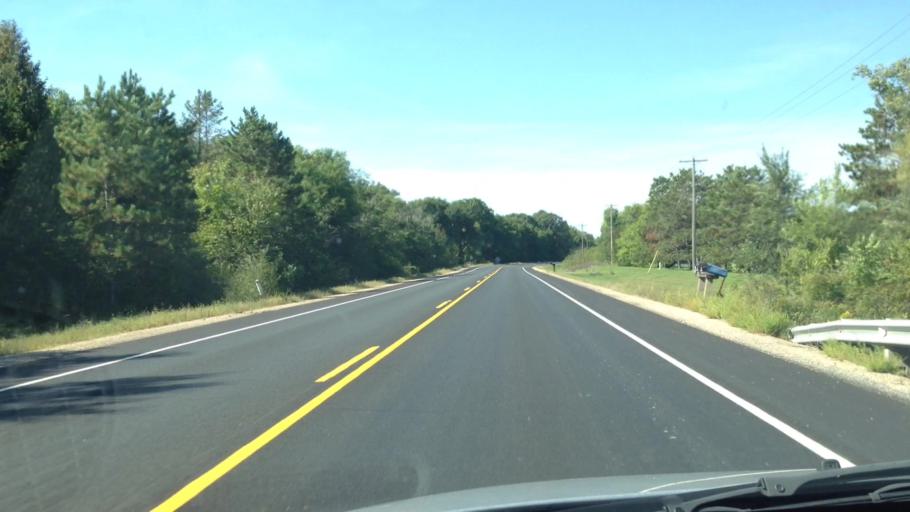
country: US
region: Minnesota
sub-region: Washington County
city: Oak Park Heights
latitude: 45.0486
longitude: -92.7828
